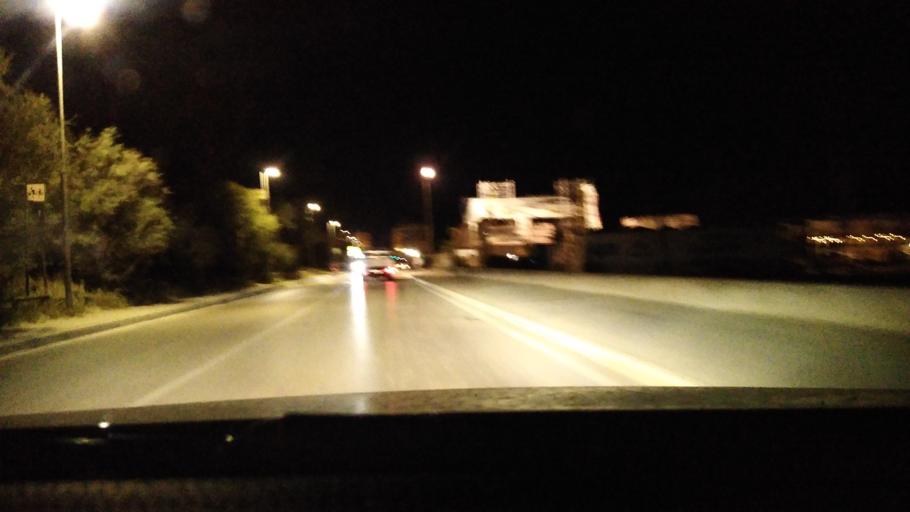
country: IT
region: Emilia-Romagna
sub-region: Provincia di Rimini
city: Bellaria-Igea Marina
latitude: 44.1262
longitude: 12.4909
